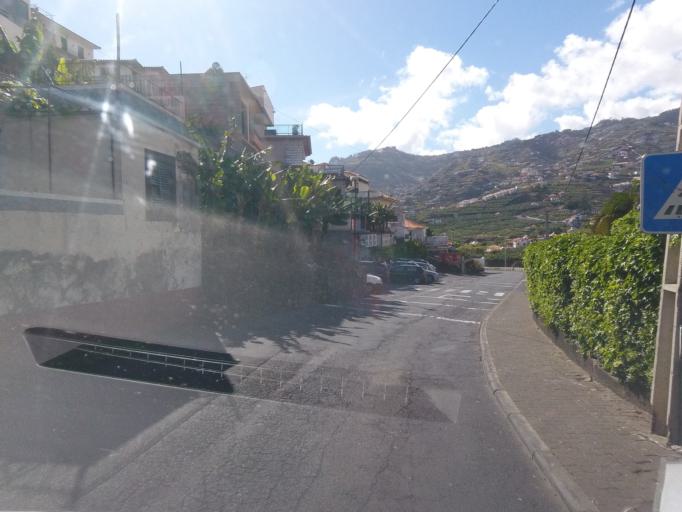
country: PT
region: Madeira
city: Camara de Lobos
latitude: 32.6538
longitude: -16.9728
